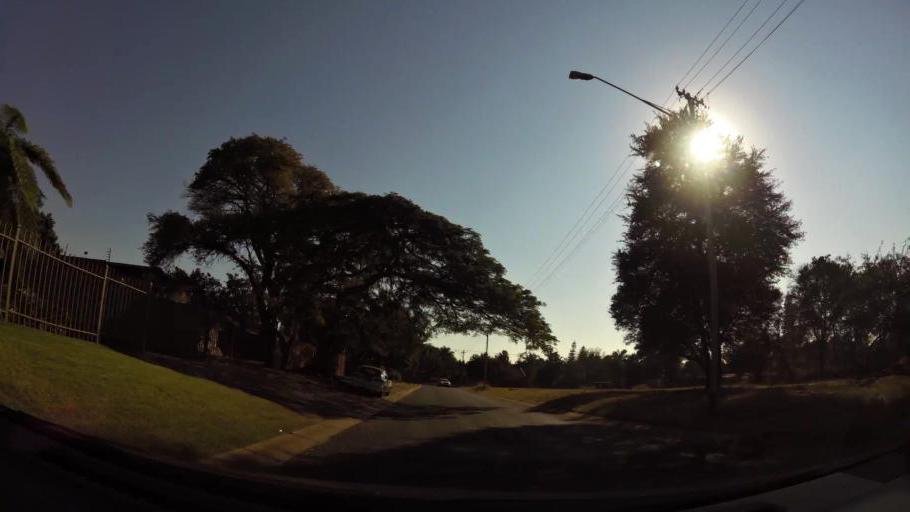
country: ZA
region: Gauteng
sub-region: City of Tshwane Metropolitan Municipality
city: Pretoria
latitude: -25.6756
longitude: 28.1568
